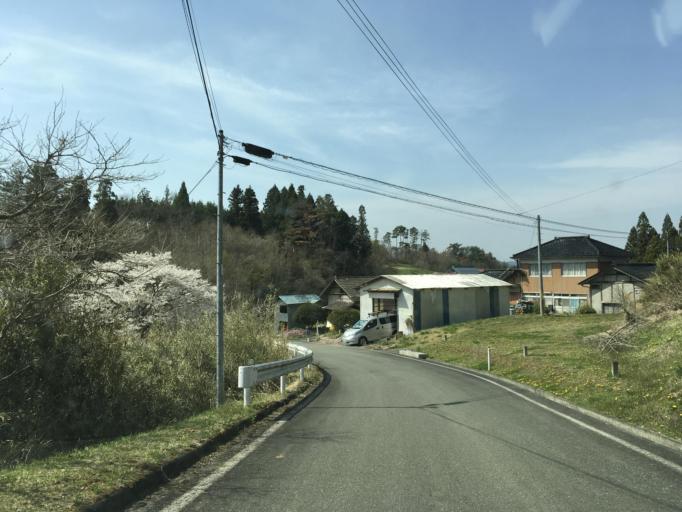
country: JP
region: Iwate
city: Ichinoseki
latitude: 38.8302
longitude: 141.3565
